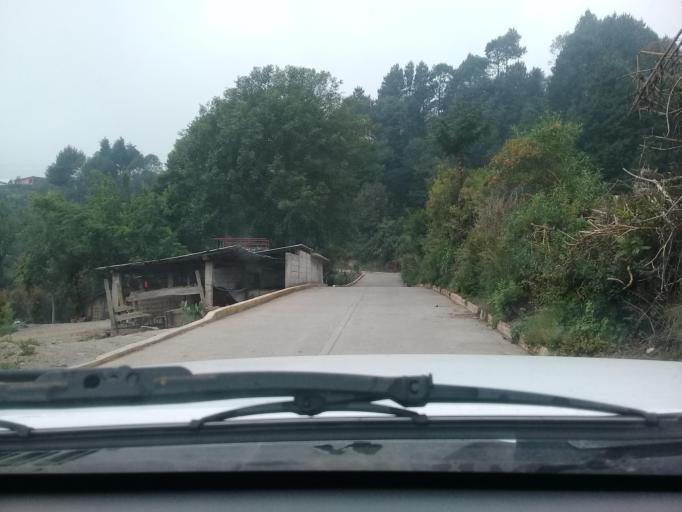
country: MX
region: Veracruz
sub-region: Mariano Escobedo
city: San Isidro el Berro
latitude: 18.9485
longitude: -97.2059
